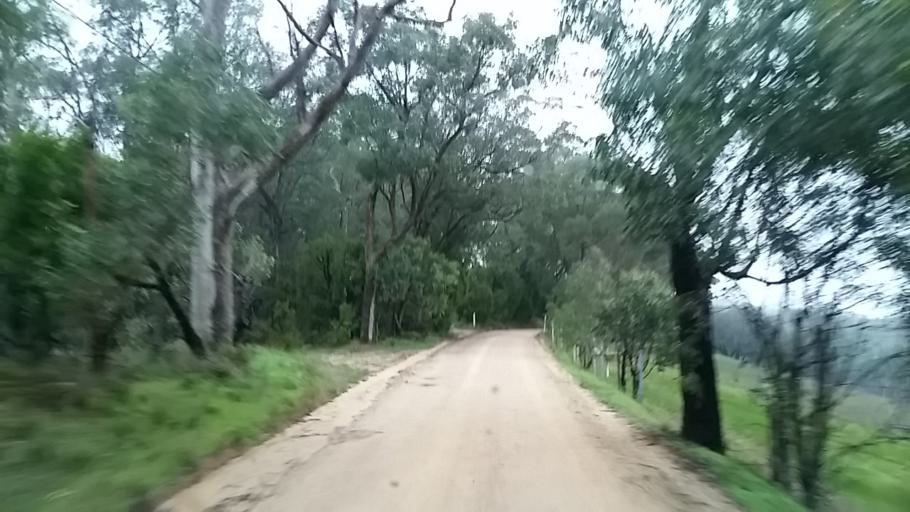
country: AU
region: South Australia
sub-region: Adelaide Hills
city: Adelaide Hills
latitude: -34.9293
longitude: 138.7423
